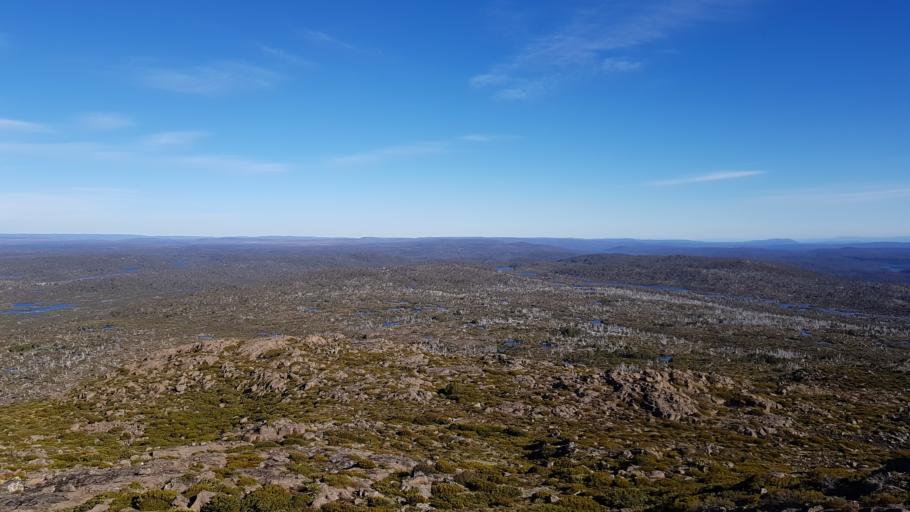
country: AU
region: Tasmania
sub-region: Kentish
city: Sheffield
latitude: -41.8207
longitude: 146.3242
